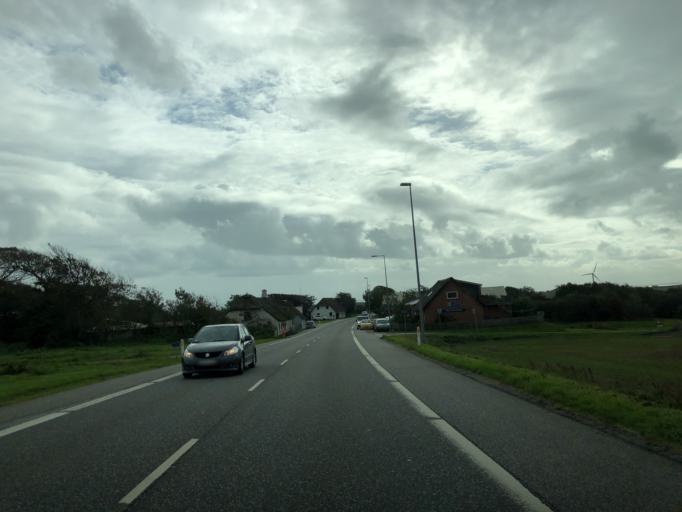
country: DK
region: North Denmark
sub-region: Thisted Kommune
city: Hurup
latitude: 56.7073
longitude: 8.4127
